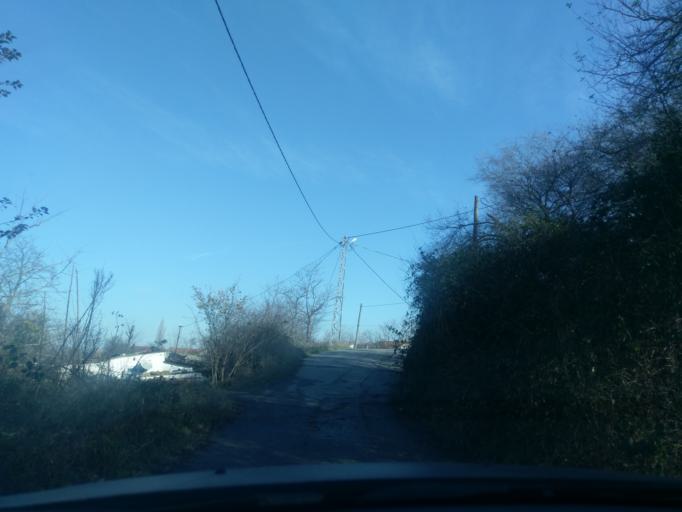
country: TR
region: Istanbul
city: Sultangazi
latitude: 41.1362
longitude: 28.8433
